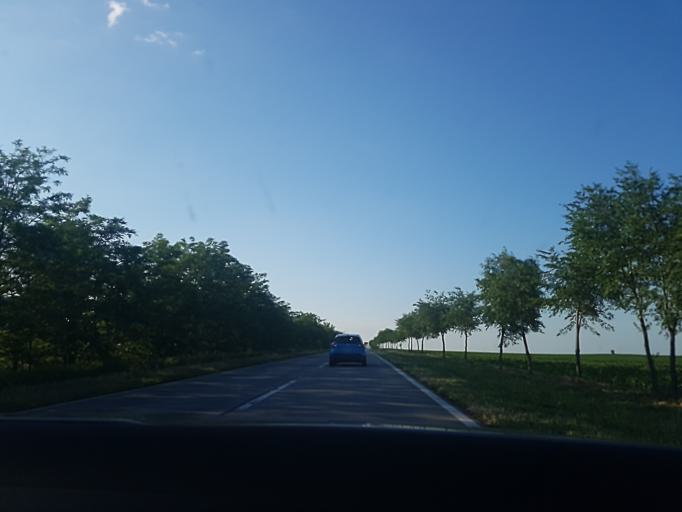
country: RO
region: Timis
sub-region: Comuna Moravita
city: Moravita
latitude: 45.2033
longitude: 21.2999
